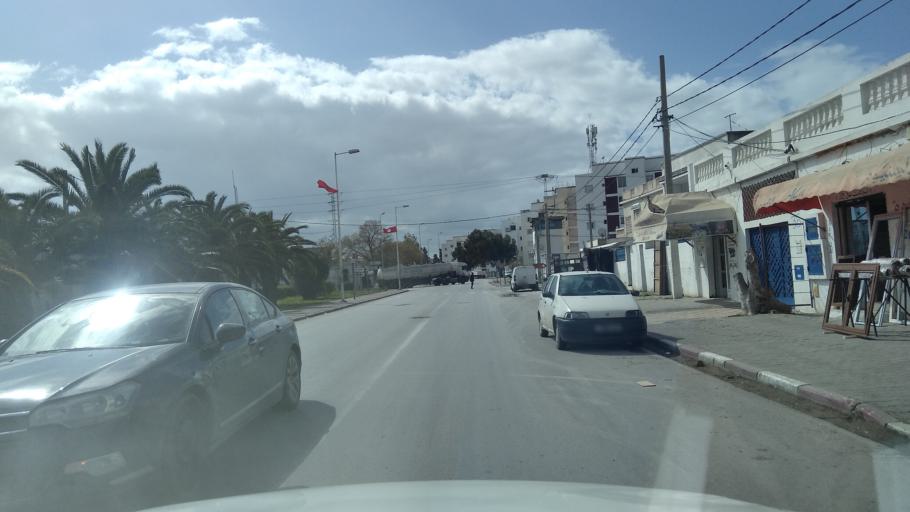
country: TN
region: Bin 'Arus
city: Ben Arous
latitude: 36.7450
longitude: 10.2260
